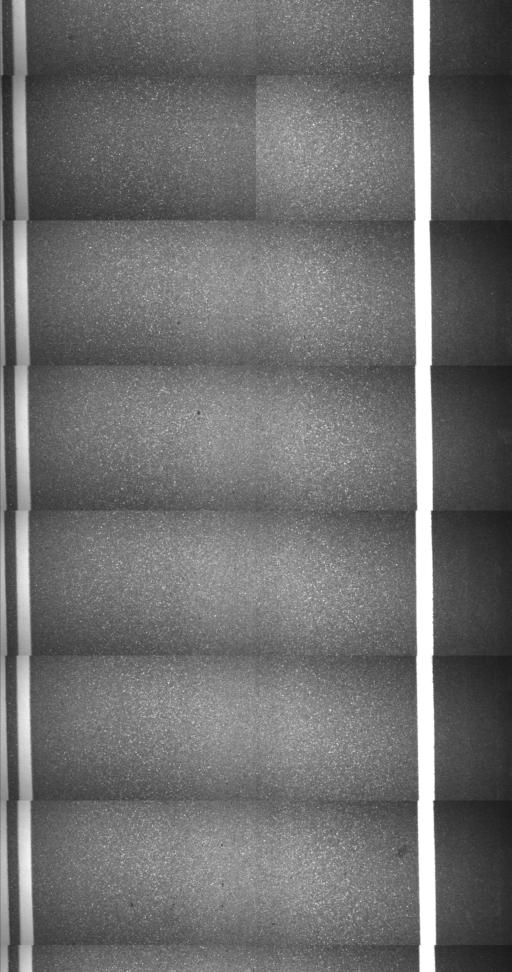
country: US
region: Vermont
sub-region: Windham County
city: Dover
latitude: 43.0326
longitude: -72.8394
